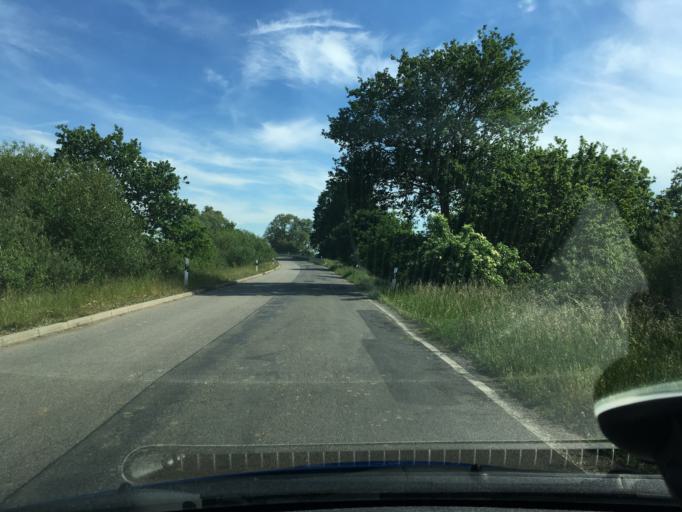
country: DE
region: Lower Saxony
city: Neu Darchau
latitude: 53.3394
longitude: 10.8601
